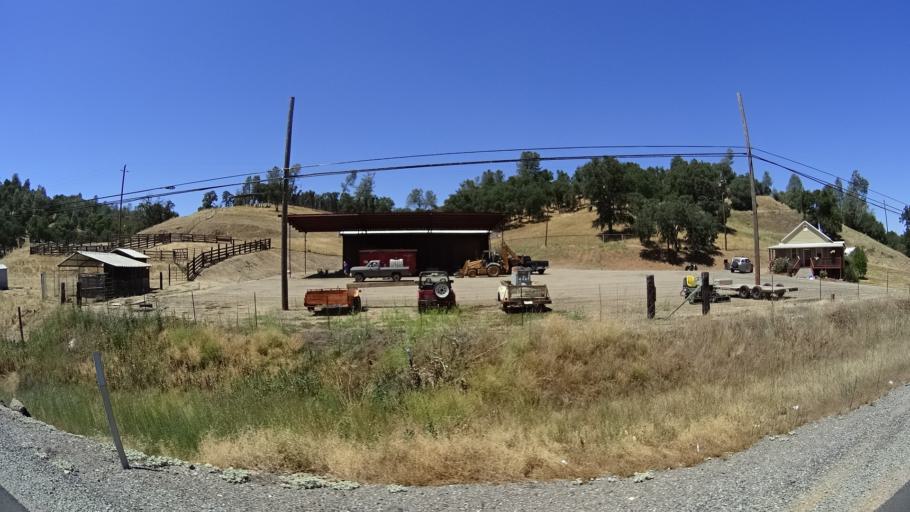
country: US
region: California
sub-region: Calaveras County
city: San Andreas
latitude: 38.2061
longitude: -120.7120
